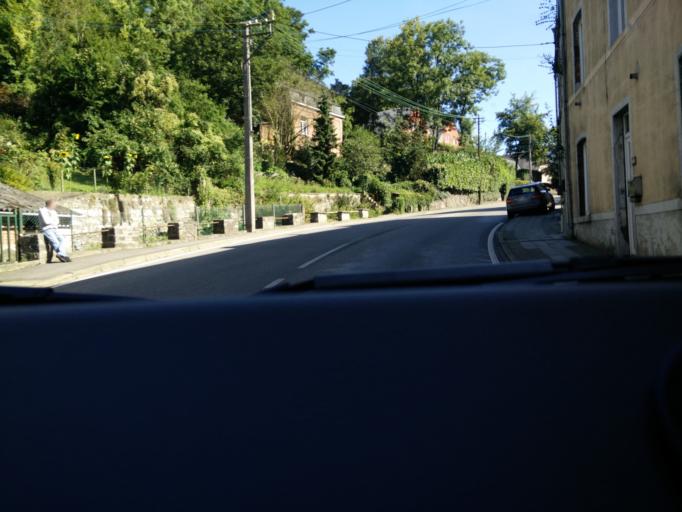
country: BE
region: Wallonia
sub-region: Province de Namur
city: Dinant
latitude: 50.2648
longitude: 4.9202
